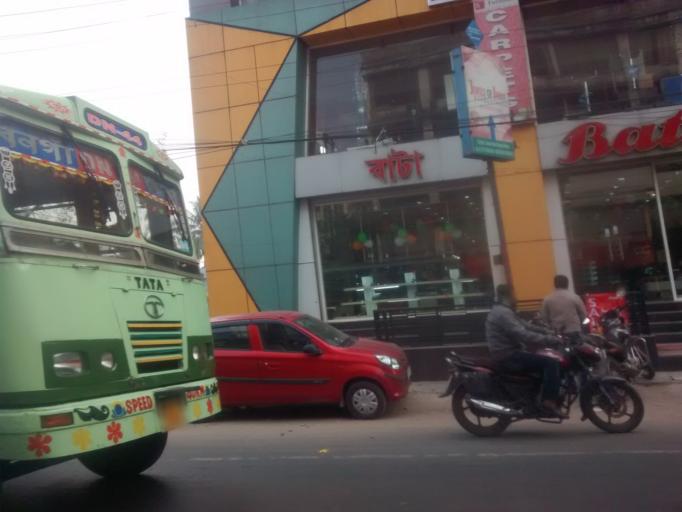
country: IN
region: West Bengal
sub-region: North 24 Parganas
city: Barasat
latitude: 22.7116
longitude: 88.4768
